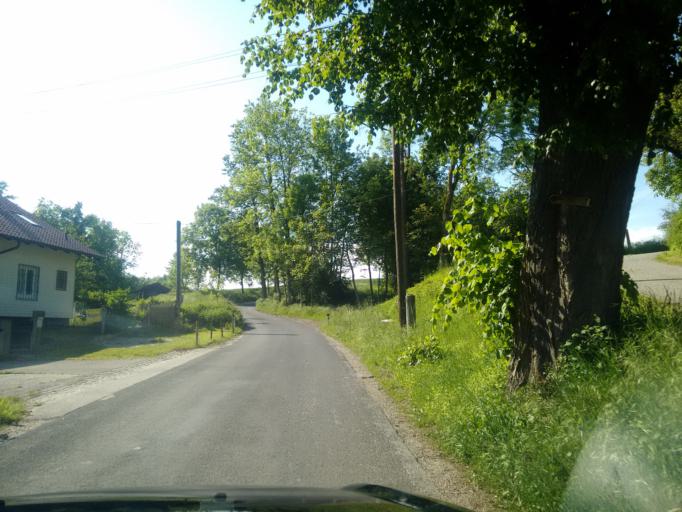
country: AT
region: Upper Austria
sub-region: Wels-Land
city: Gunskirchen
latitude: 48.1705
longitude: 13.9650
